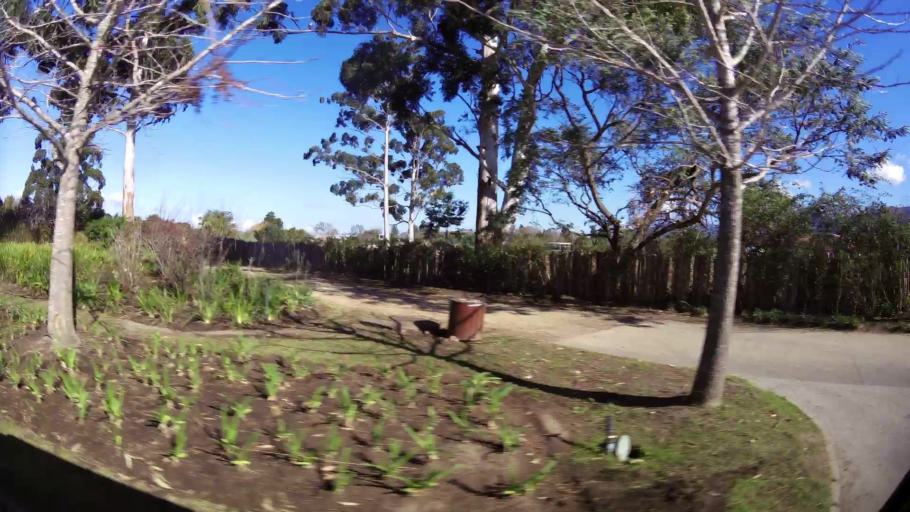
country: ZA
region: Western Cape
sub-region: Eden District Municipality
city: George
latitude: -33.9509
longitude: 22.4131
